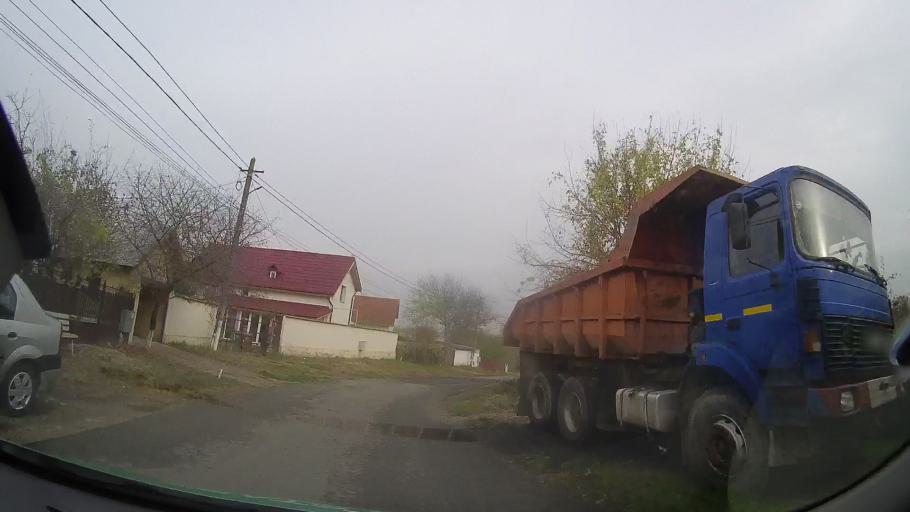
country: RO
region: Ilfov
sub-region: Comuna Ciolpani
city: Ciolpani
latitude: 44.7453
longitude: 26.1136
